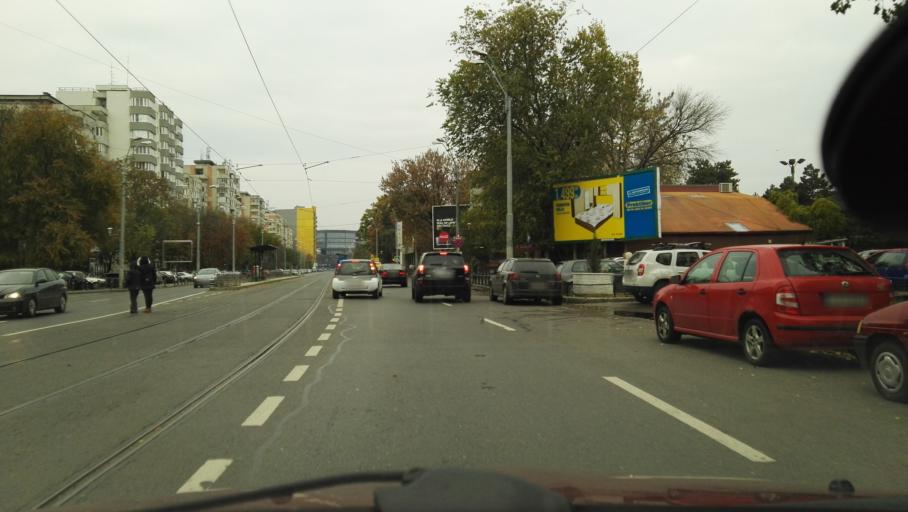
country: RO
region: Bucuresti
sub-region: Municipiul Bucuresti
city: Bucuresti
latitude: 44.3997
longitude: 26.1060
